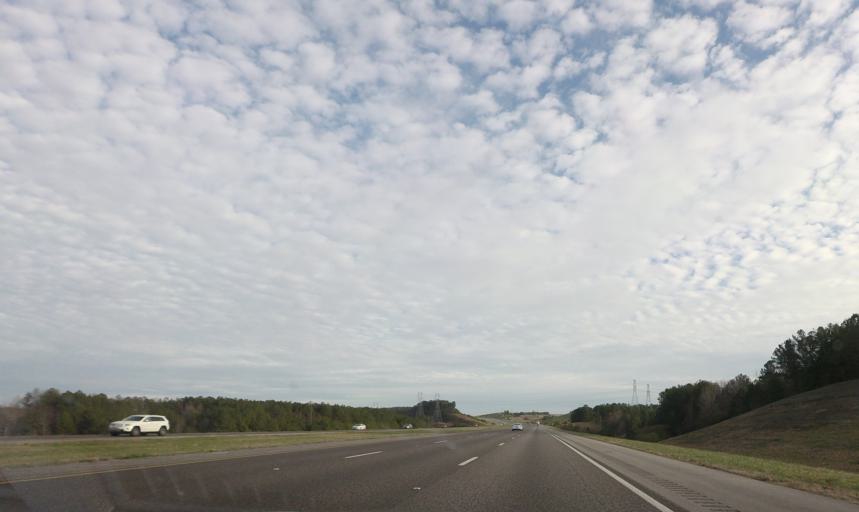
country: US
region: Alabama
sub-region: Jefferson County
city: Graysville
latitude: 33.6562
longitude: -87.0118
